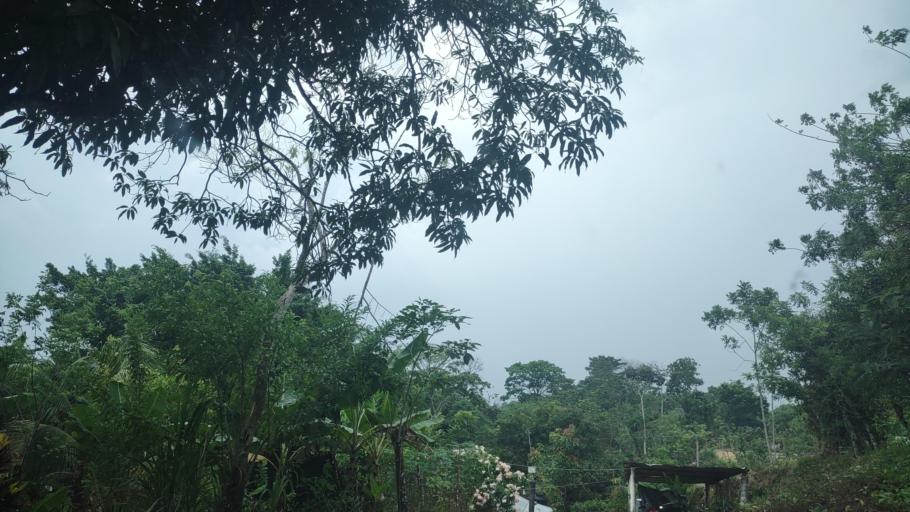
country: MX
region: Veracruz
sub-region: Uxpanapa
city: Poblado 10
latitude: 17.4526
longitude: -94.1001
